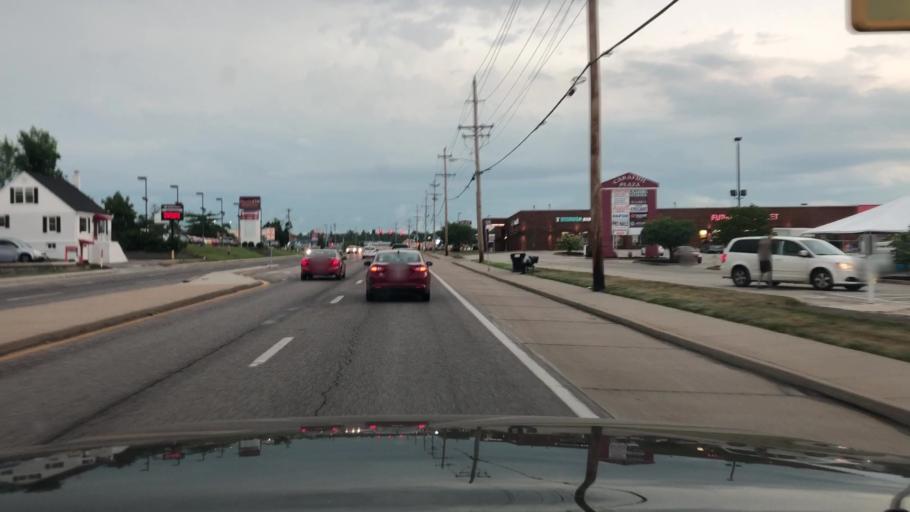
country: US
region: Missouri
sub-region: Saint Louis County
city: Bridgeton
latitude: 38.7504
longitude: -90.4256
